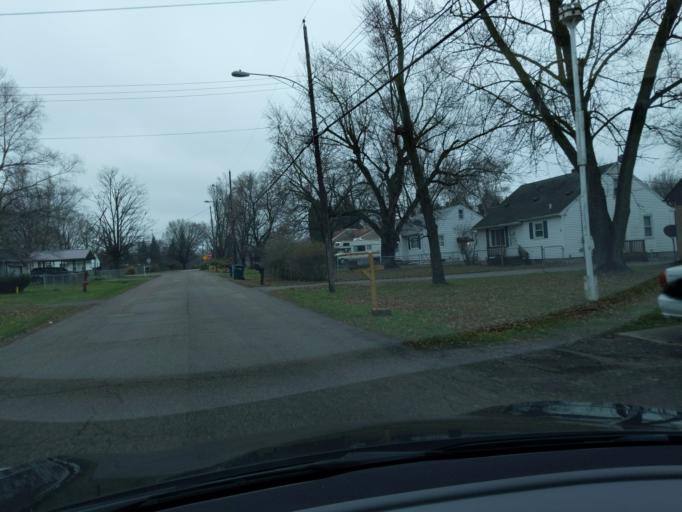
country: US
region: Michigan
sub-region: Ingham County
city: Lansing
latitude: 42.6817
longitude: -84.5714
